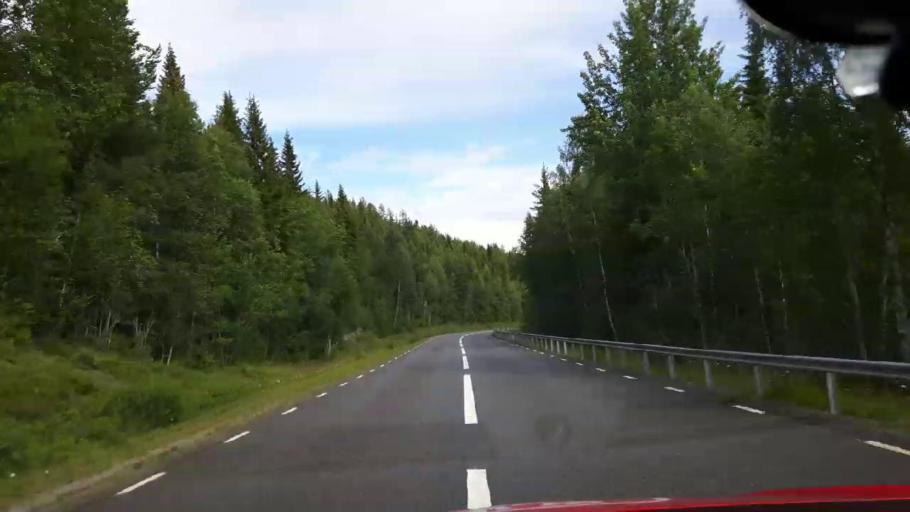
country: SE
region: Jaemtland
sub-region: Stroemsunds Kommun
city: Stroemsund
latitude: 64.3385
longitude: 14.9101
